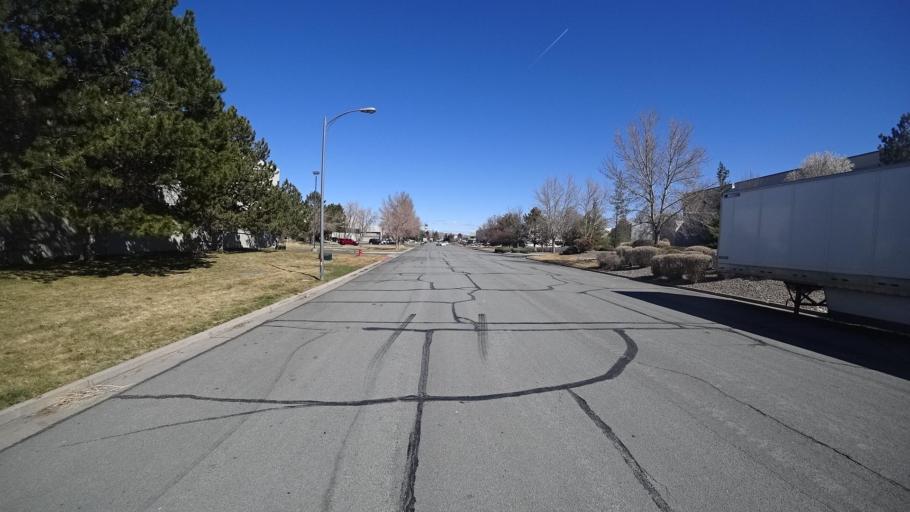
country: US
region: Nevada
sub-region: Washoe County
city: Sparks
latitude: 39.4867
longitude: -119.7628
